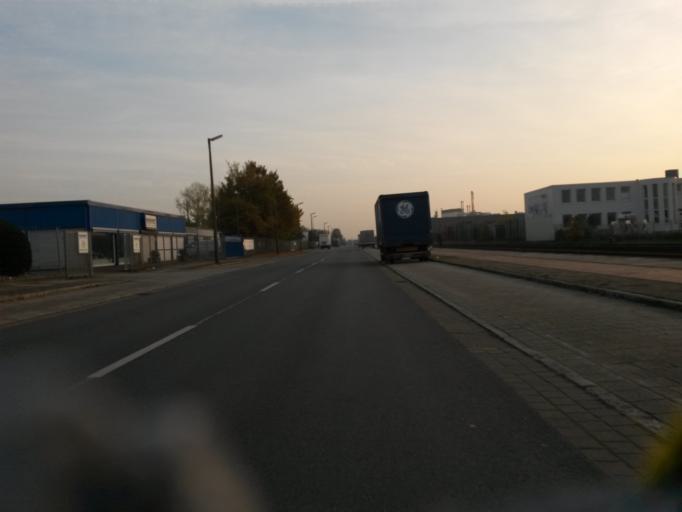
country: DE
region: Bremen
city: Bremen
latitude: 53.0469
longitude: 8.8838
